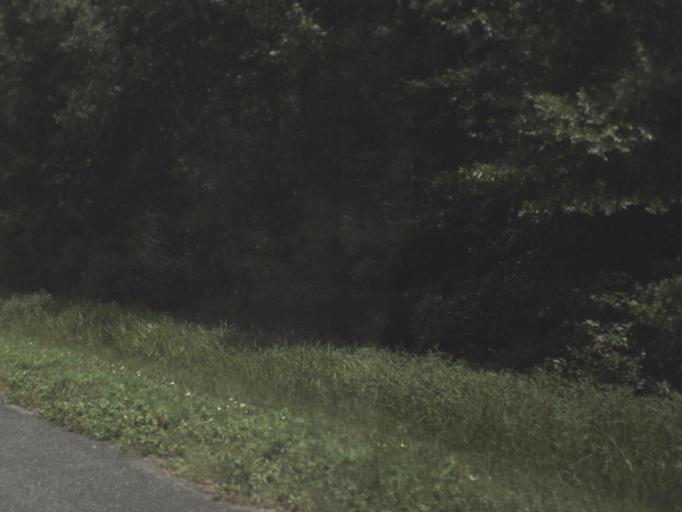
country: US
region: Florida
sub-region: Taylor County
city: Steinhatchee
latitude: 29.8497
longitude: -83.3104
